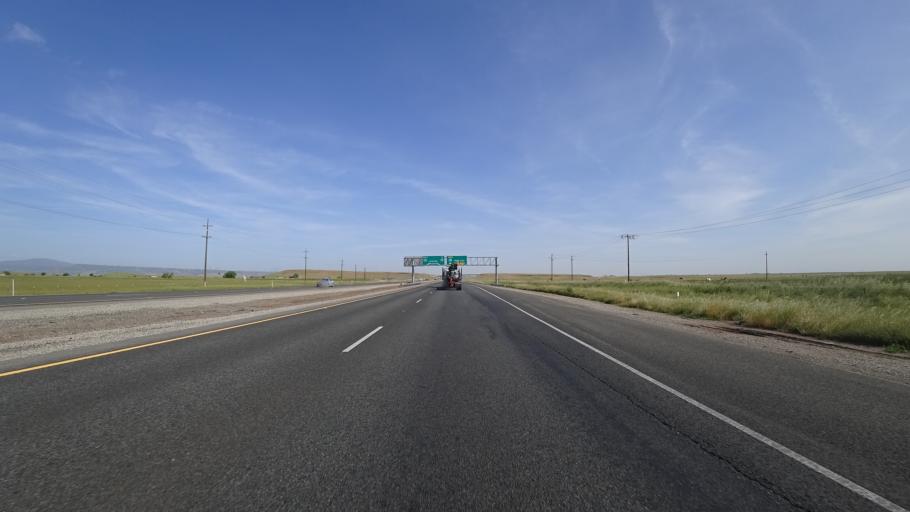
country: US
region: California
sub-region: Butte County
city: Durham
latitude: 39.6312
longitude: -121.7037
